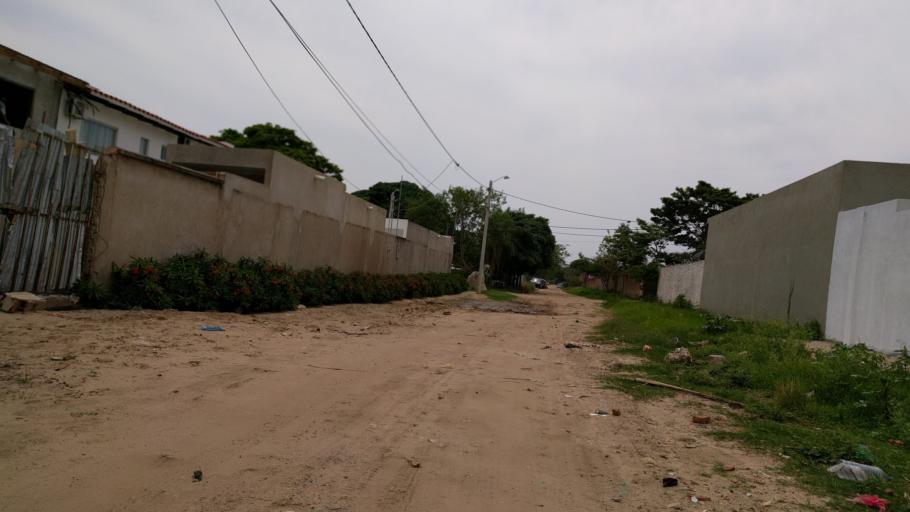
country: BO
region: Santa Cruz
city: Santa Cruz de la Sierra
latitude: -17.8159
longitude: -63.2334
